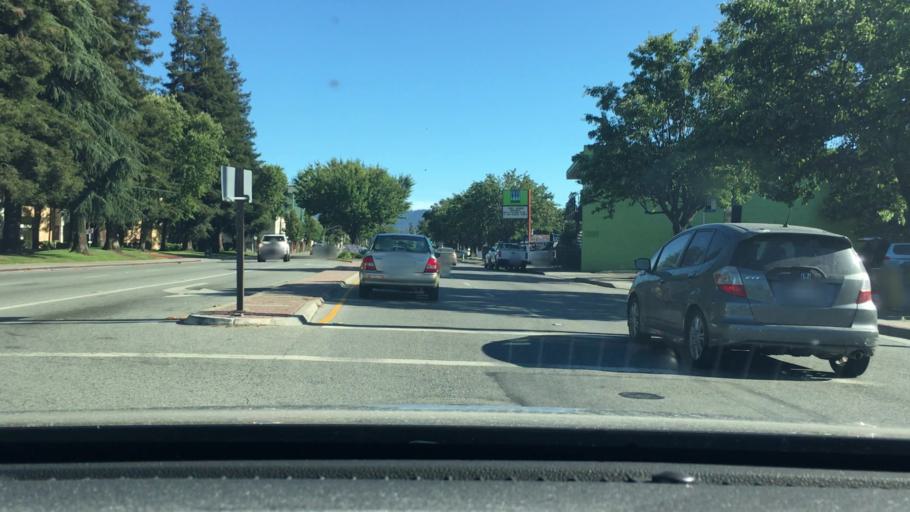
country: US
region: California
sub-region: San Mateo County
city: Redwood City
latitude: 37.4715
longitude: -122.2231
